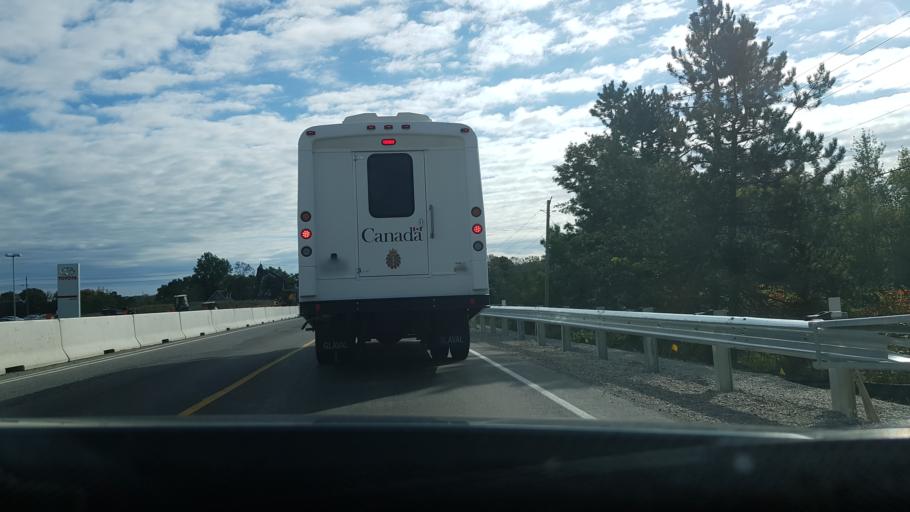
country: CA
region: Ontario
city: Orillia
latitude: 44.6126
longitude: -79.4672
